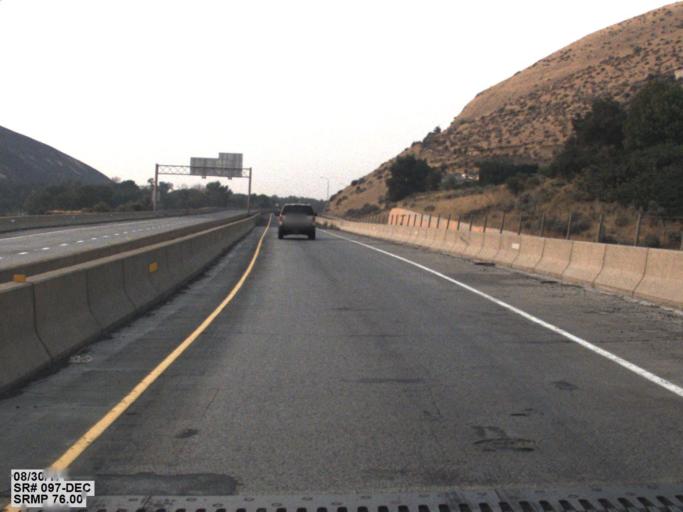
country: US
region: Washington
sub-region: Yakima County
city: Union Gap
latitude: 46.5373
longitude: -120.4746
